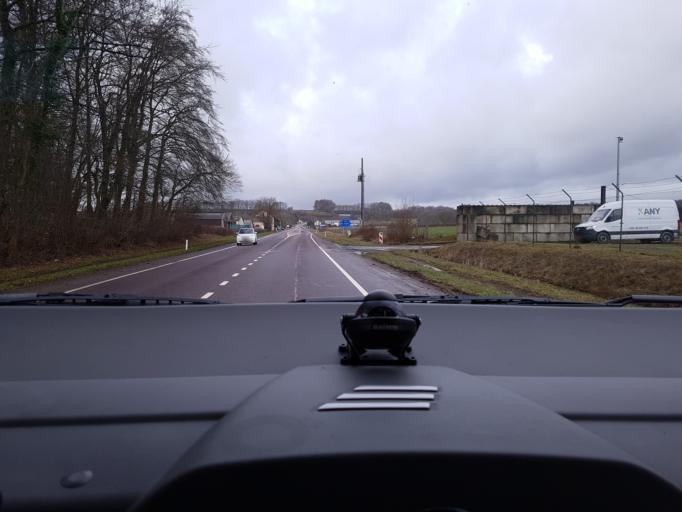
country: LU
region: Luxembourg
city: Eischen
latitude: 49.6580
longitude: 5.8699
